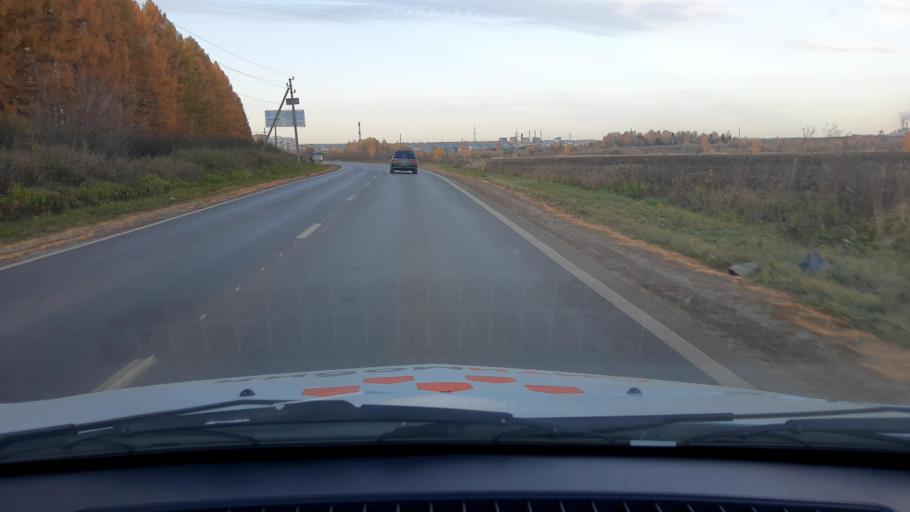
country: RU
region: Bashkortostan
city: Iglino
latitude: 54.7447
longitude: 56.2539
